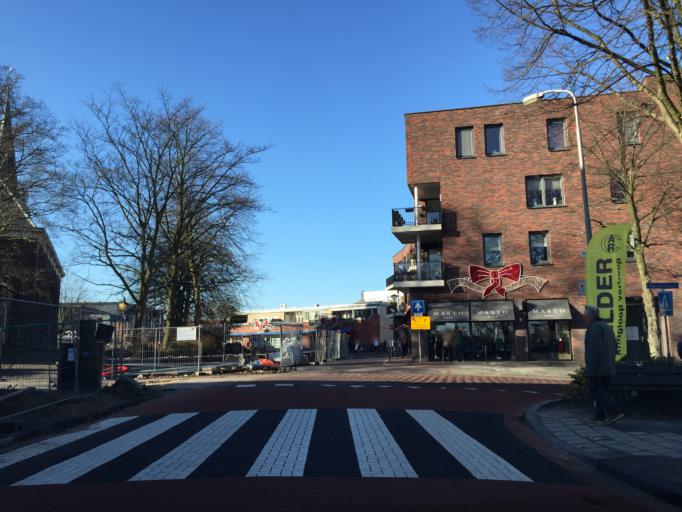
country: NL
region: South Holland
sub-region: Gemeente Lansingerland
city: Berkel en Rodenrijs
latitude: 51.9933
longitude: 4.4797
